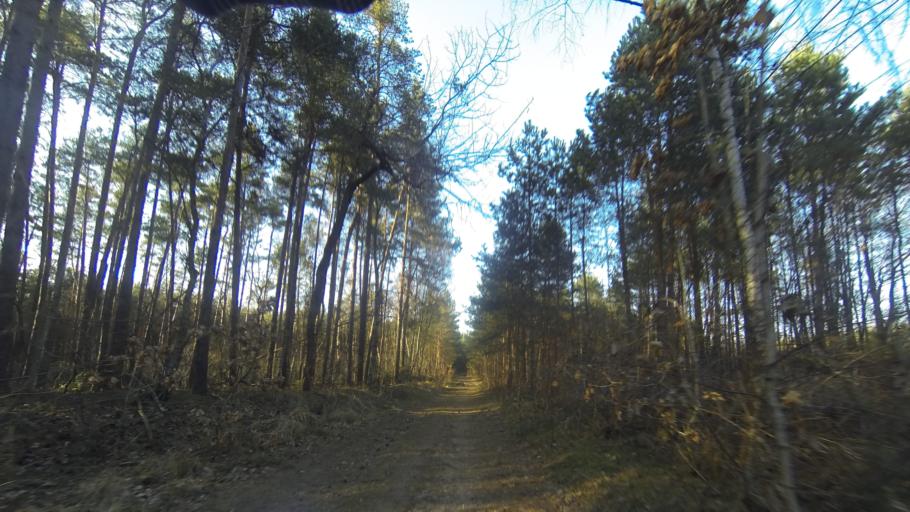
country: DE
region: Saxony
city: Ottendorf-Okrilla
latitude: 51.2028
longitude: 13.8028
